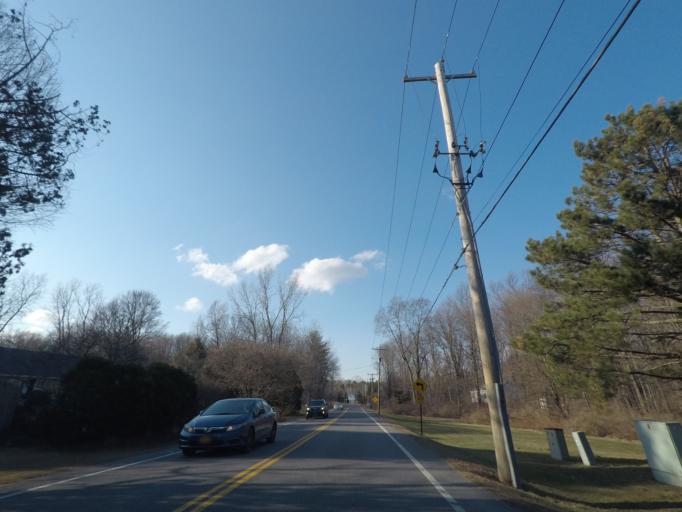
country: US
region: New York
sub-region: Schenectady County
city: Niskayuna
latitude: 42.8306
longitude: -73.7898
